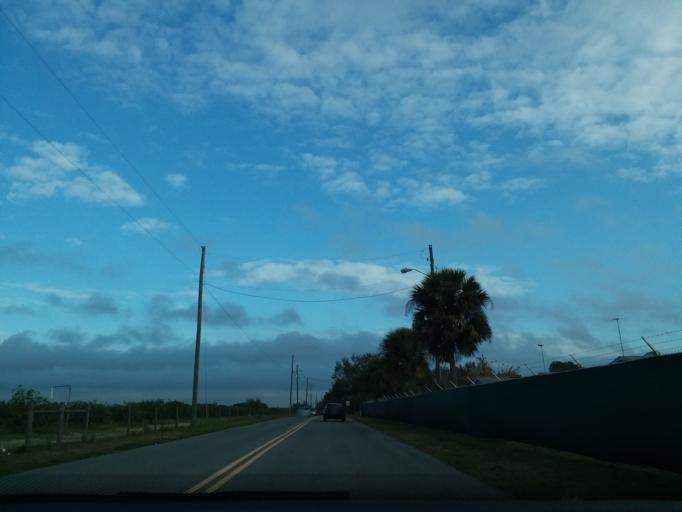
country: US
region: Florida
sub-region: Polk County
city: Haines City
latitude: 28.1160
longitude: -81.6526
